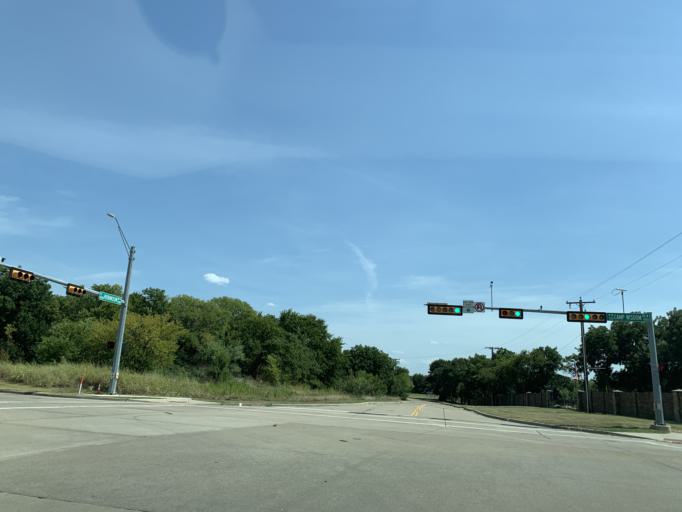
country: US
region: Texas
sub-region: Dallas County
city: Cedar Hill
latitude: 32.6439
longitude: -97.0142
